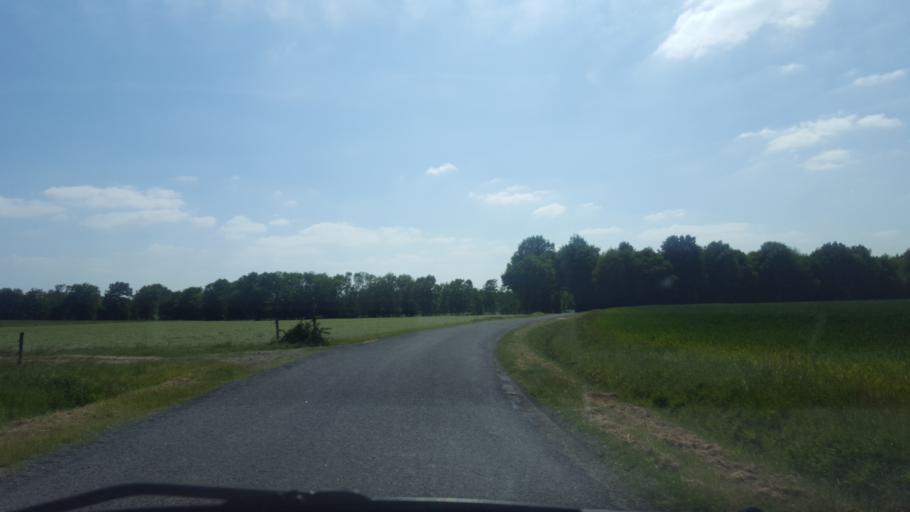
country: FR
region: Pays de la Loire
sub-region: Departement de la Loire-Atlantique
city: Saint-Philbert-de-Grand-Lieu
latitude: 47.0305
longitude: -1.6133
